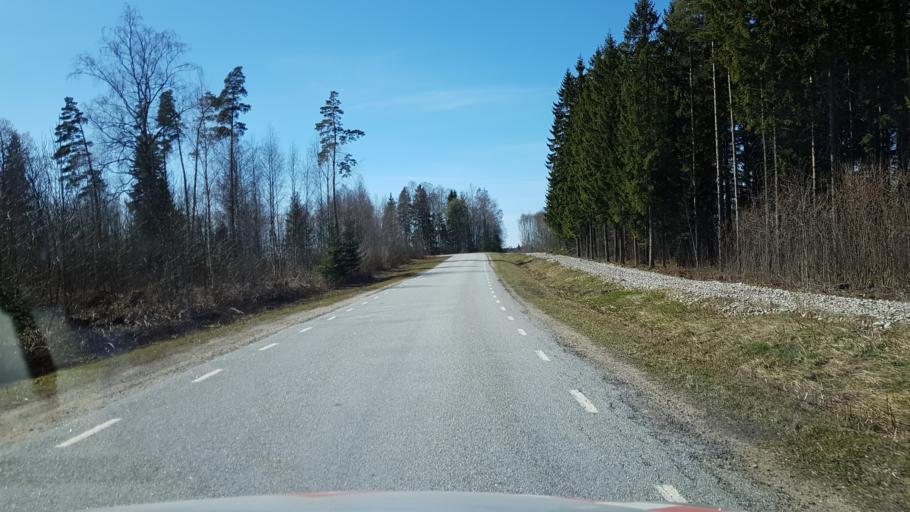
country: EE
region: Laeaene-Virumaa
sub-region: Viru-Nigula vald
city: Kunda
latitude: 59.3379
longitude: 26.6583
